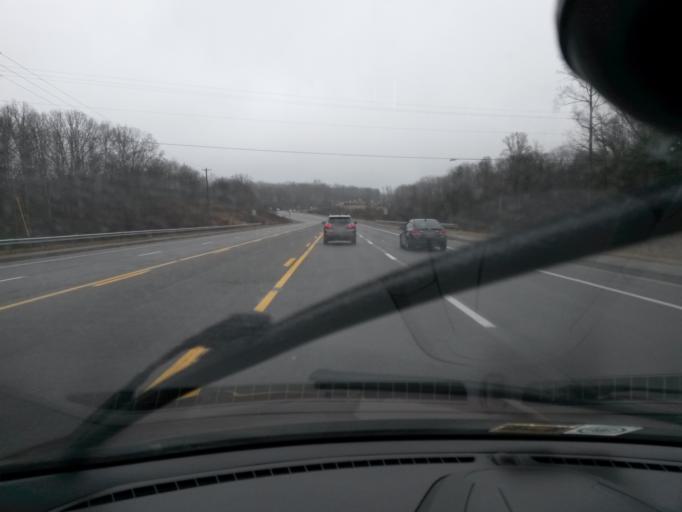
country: US
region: West Virginia
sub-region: Raleigh County
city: Beckley
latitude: 37.7793
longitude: -81.1552
